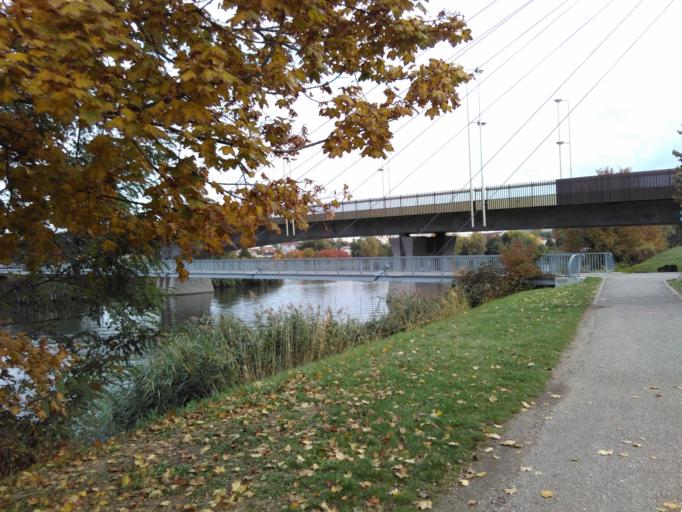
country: FR
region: Lorraine
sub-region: Departement de Meurthe-et-Moselle
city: Tomblaine
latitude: 48.6908
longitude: 6.2037
